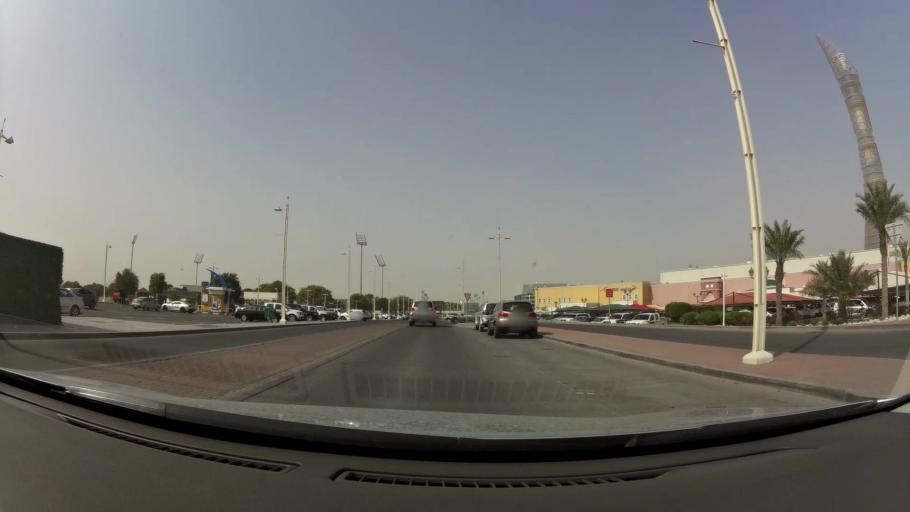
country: QA
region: Baladiyat ar Rayyan
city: Ar Rayyan
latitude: 25.2602
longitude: 51.4403
